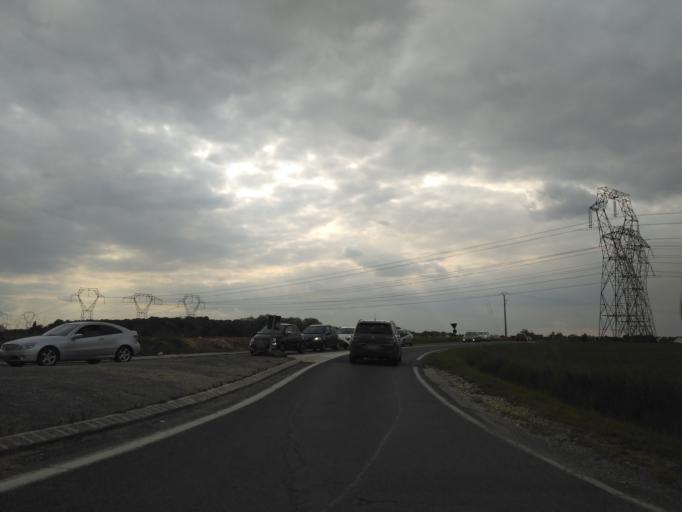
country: FR
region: Ile-de-France
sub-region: Departement de Seine-et-Marne
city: Voisenon
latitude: 48.5682
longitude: 2.6758
